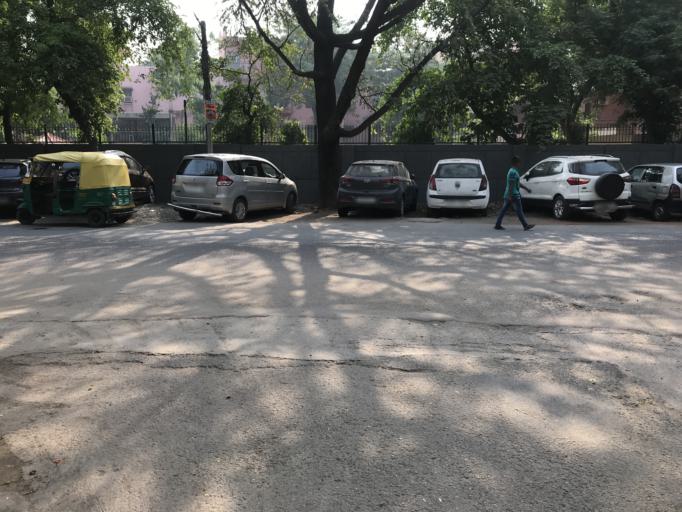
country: IN
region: Uttar Pradesh
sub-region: Gautam Buddha Nagar
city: Noida
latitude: 28.5260
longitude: 77.2633
